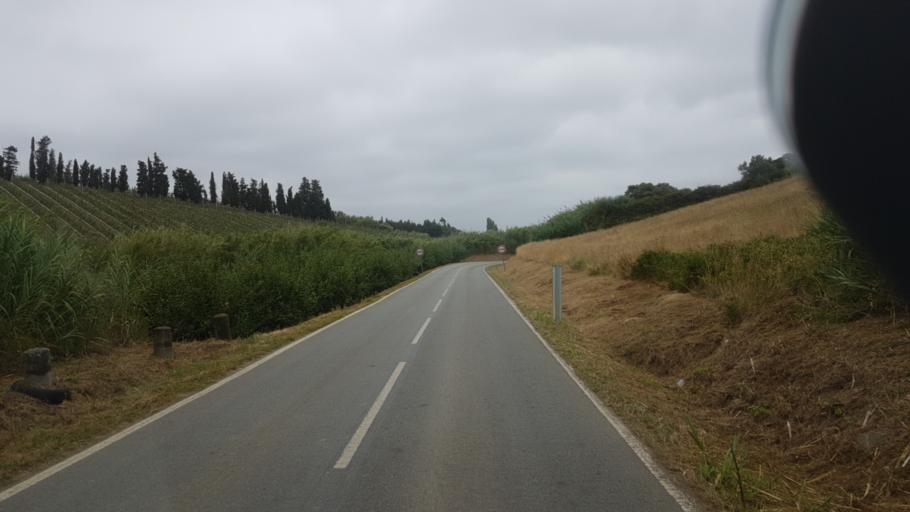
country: PT
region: Leiria
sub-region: Bombarral
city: Bombarral
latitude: 39.2916
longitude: -9.1995
